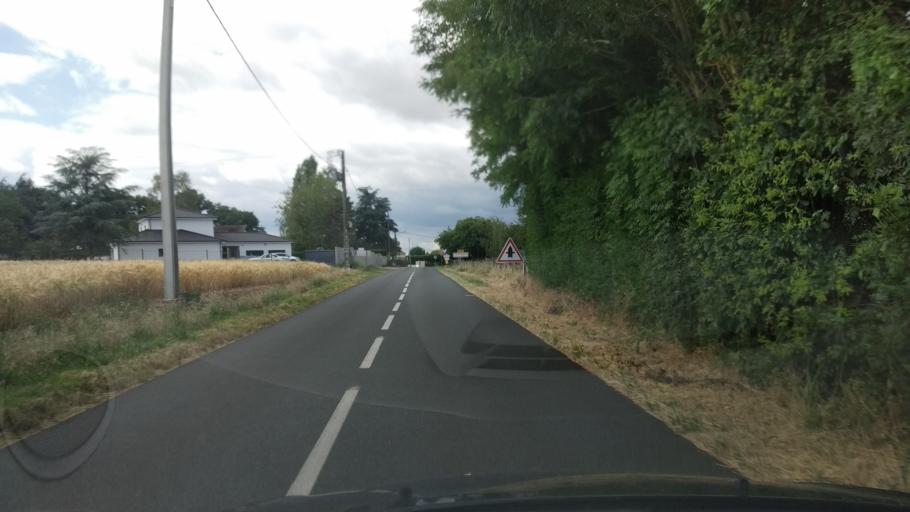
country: FR
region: Poitou-Charentes
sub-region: Departement de la Vienne
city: Vouille
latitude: 46.6280
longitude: 0.1922
